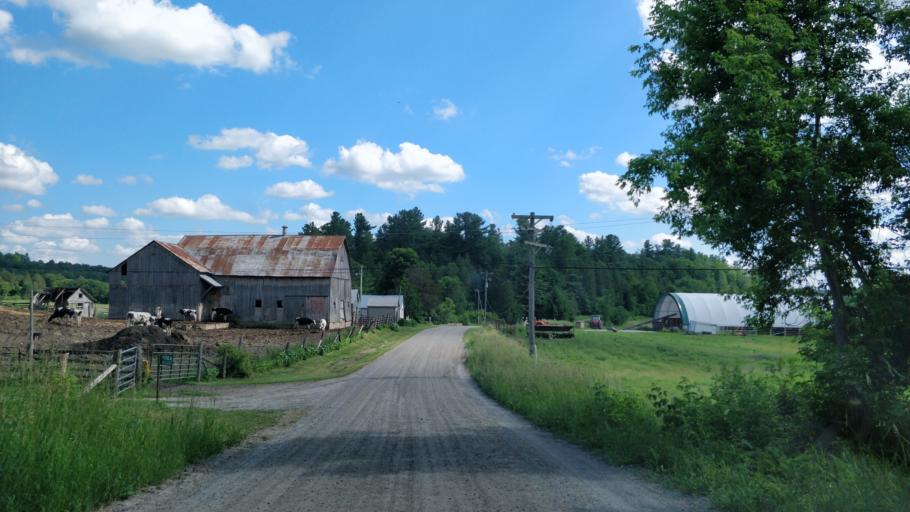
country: CA
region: Ontario
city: Perth
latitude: 44.6786
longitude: -76.5295
